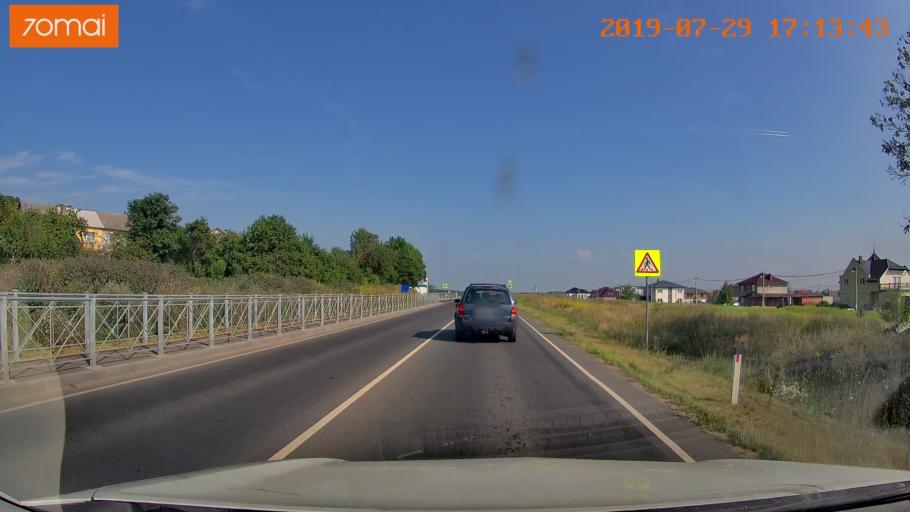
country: RU
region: Kaliningrad
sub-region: Gorod Kaliningrad
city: Kaliningrad
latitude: 54.7858
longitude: 20.4052
